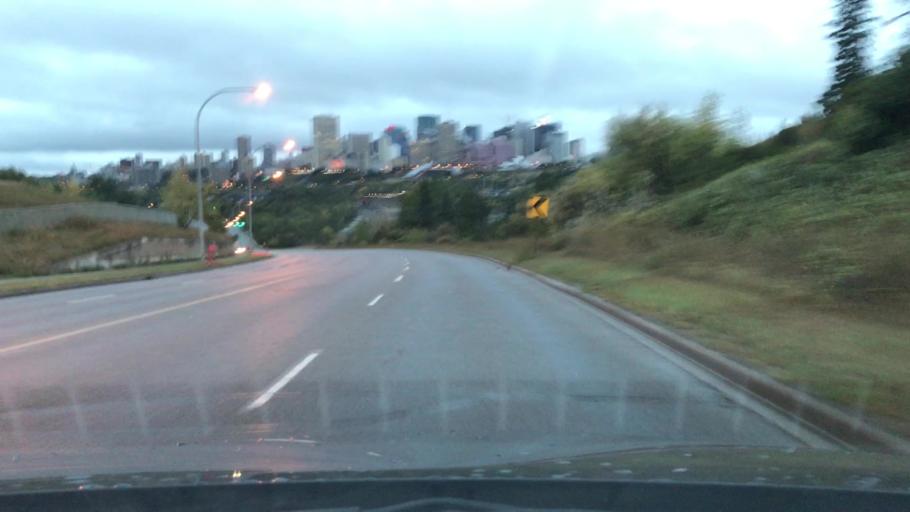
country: CA
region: Alberta
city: Edmonton
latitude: 53.5383
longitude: -113.4602
